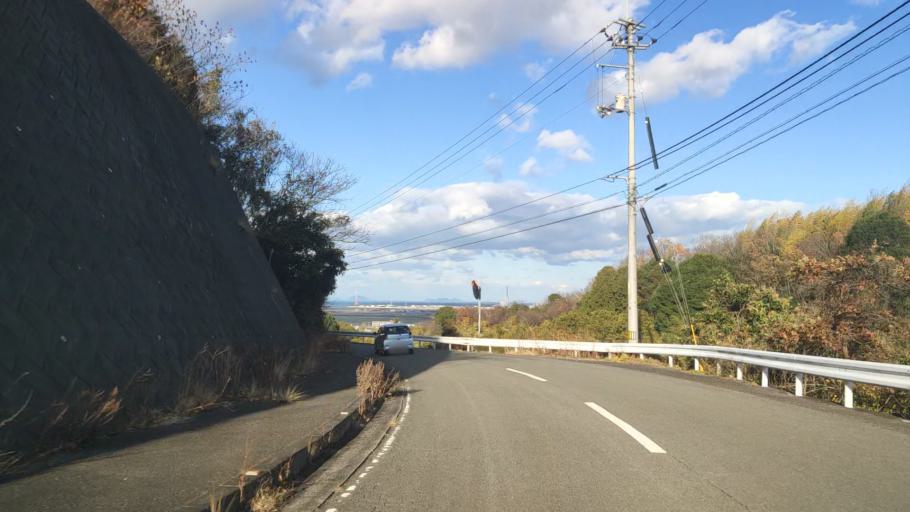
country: JP
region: Ehime
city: Saijo
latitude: 33.8844
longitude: 133.1305
